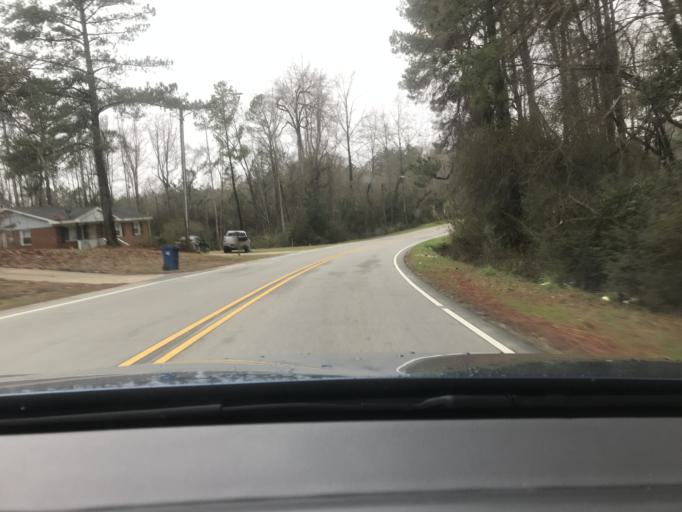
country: US
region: North Carolina
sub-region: Hoke County
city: Rockfish
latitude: 35.0231
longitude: -79.0082
